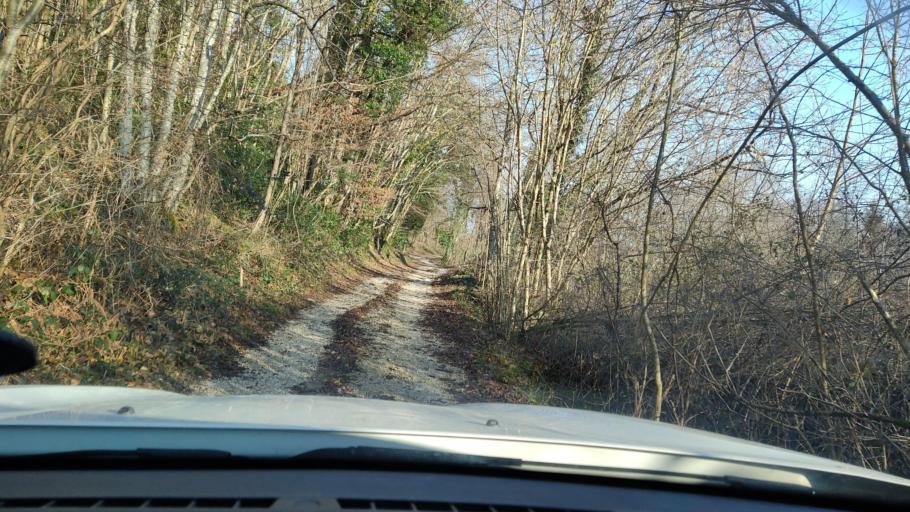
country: FR
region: Rhone-Alpes
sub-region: Departement de la Savoie
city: Le Bourget-du-Lac
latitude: 45.6723
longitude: 5.8517
